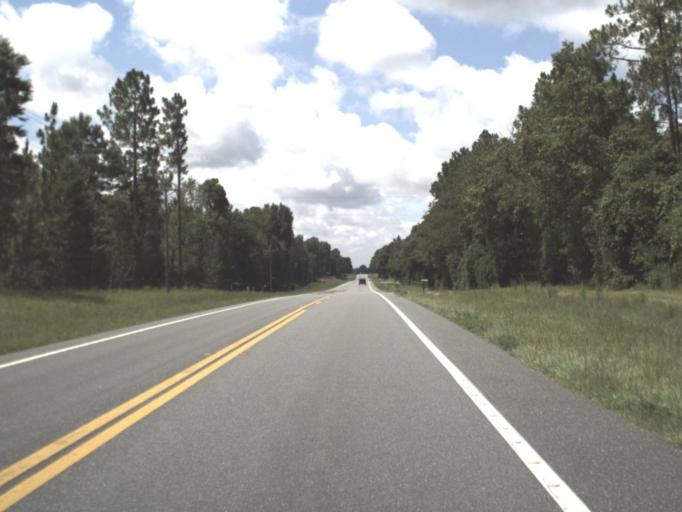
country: US
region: Florida
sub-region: Alachua County
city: High Springs
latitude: 29.8808
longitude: -82.8598
